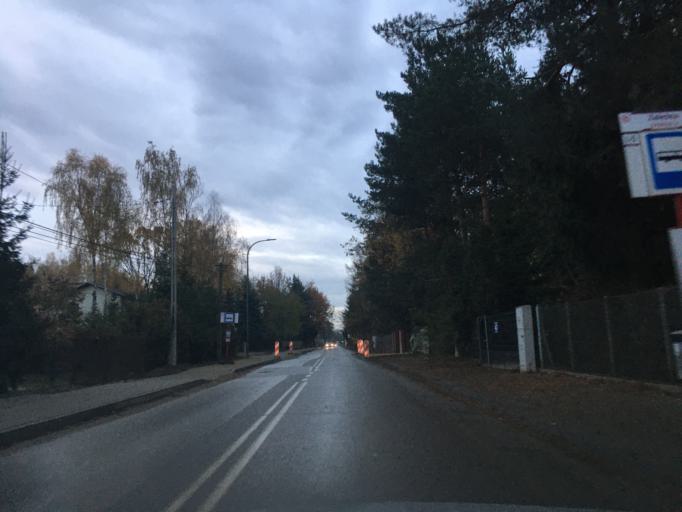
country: PL
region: Masovian Voivodeship
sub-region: Powiat piaseczynski
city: Piaseczno
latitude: 52.0593
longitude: 20.9804
